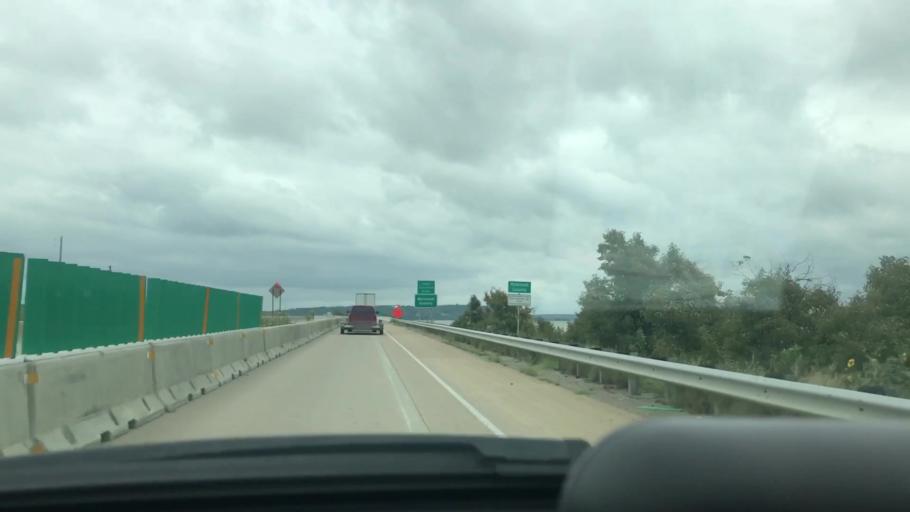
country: US
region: Oklahoma
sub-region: McIntosh County
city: Eufaula
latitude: 35.2217
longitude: -95.6068
